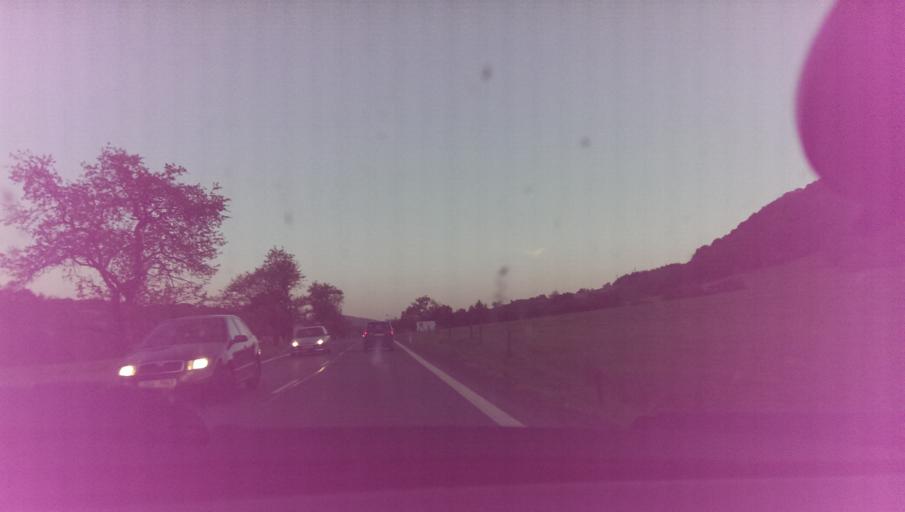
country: CZ
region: Zlin
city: Valasska Polanka
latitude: 49.2961
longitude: 18.0012
